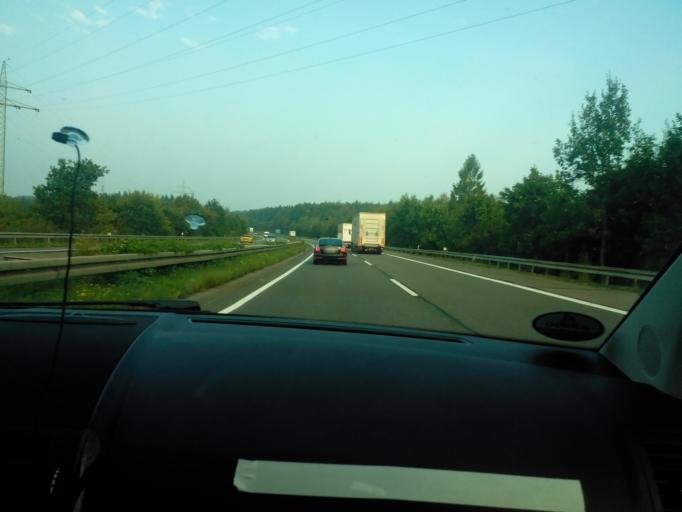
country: DE
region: Saarland
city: Schwalbach
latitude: 49.3272
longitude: 6.8368
